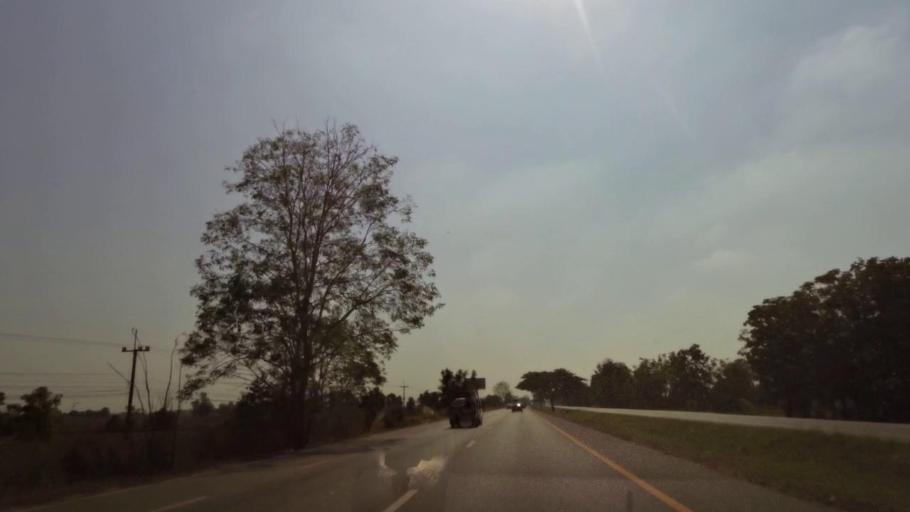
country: TH
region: Phichit
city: Wachira Barami
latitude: 16.4691
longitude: 100.1474
